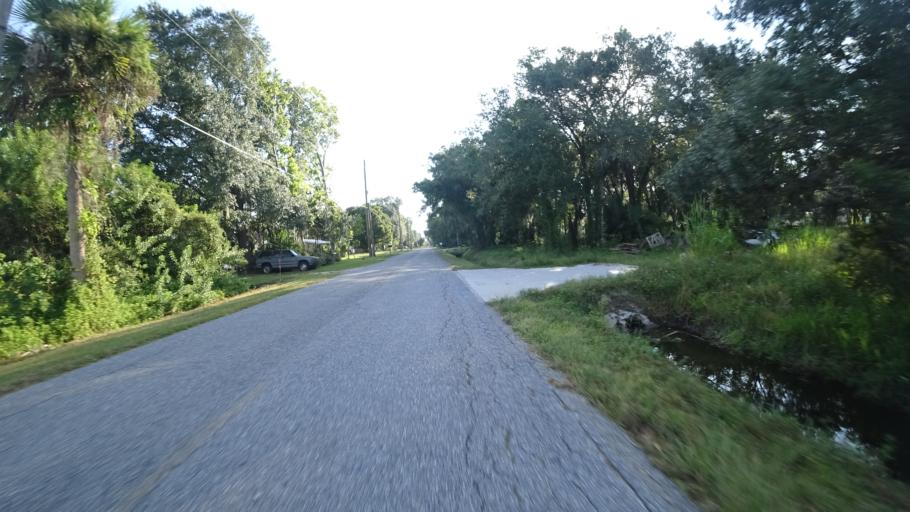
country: US
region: Florida
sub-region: Manatee County
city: Samoset
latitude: 27.4692
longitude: -82.5031
